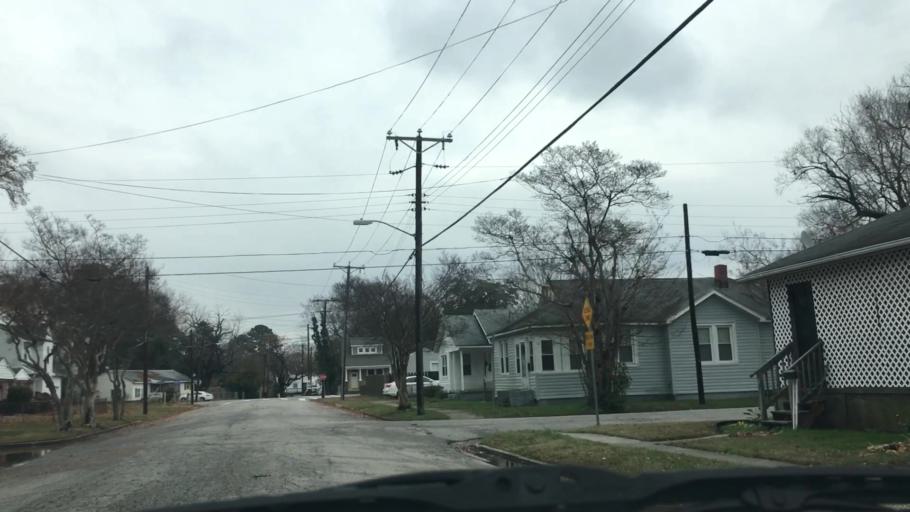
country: US
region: Virginia
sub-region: City of Norfolk
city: Norfolk
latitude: 36.8754
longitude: -76.2480
